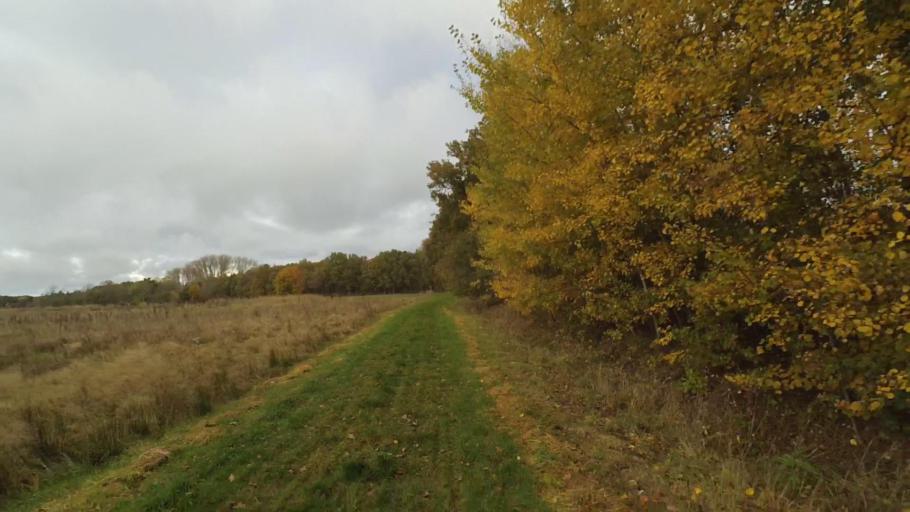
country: NL
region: Gelderland
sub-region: Gemeente Barneveld
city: Terschuur
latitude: 52.1425
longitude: 5.5241
